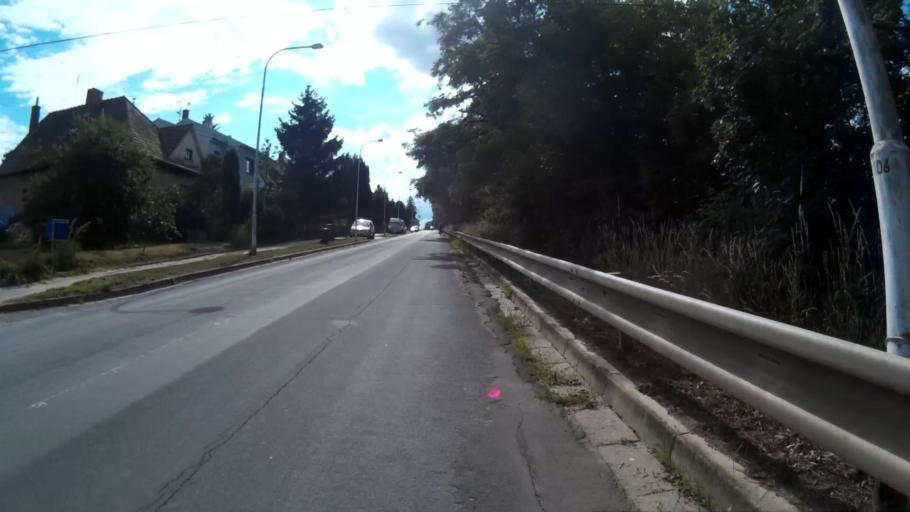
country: CZ
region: South Moravian
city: Strelice
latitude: 49.1535
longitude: 16.4830
